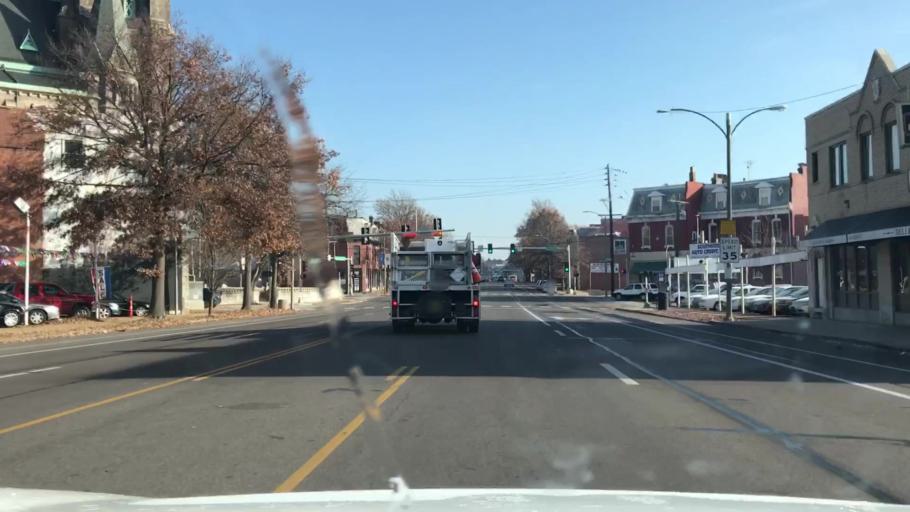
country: US
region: Missouri
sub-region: City of Saint Louis
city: St. Louis
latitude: 38.6034
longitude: -90.2265
